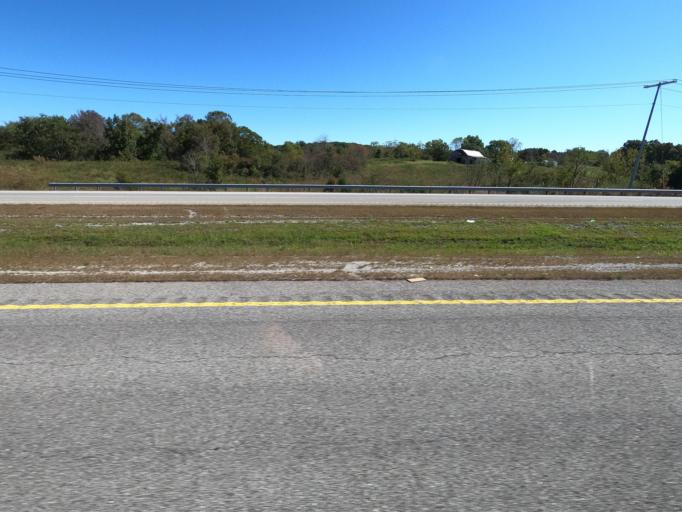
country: US
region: Tennessee
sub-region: Maury County
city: Mount Pleasant
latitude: 35.4599
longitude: -87.2686
